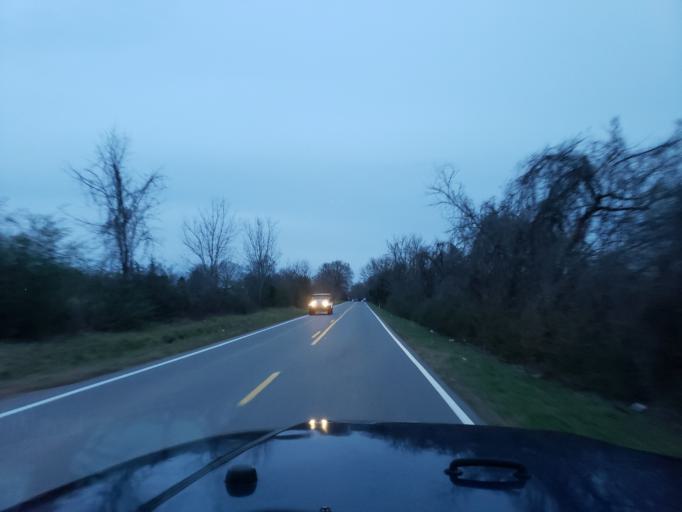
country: US
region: North Carolina
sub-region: Cleveland County
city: White Plains
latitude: 35.2115
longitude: -81.4537
